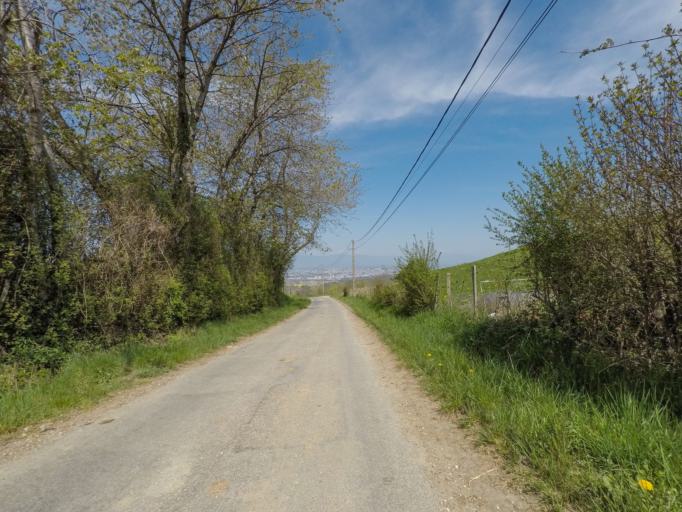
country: FR
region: Rhone-Alpes
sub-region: Departement de la Haute-Savoie
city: Archamps
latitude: 46.1211
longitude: 6.1378
